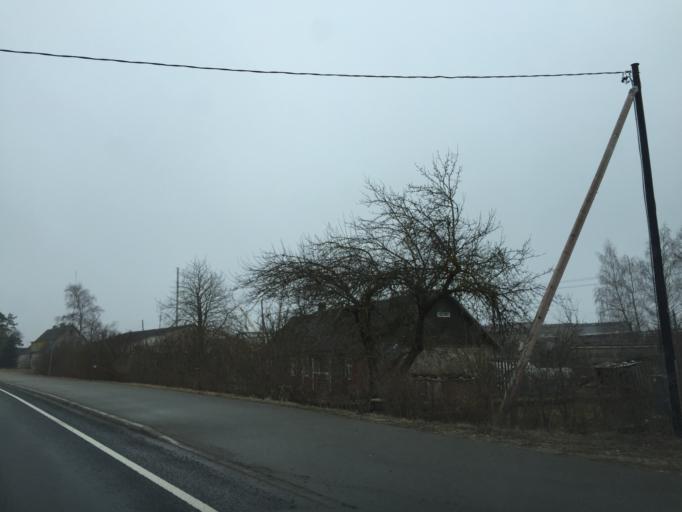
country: EE
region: Laeaene
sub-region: Lihula vald
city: Lihula
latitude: 58.5807
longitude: 23.5242
